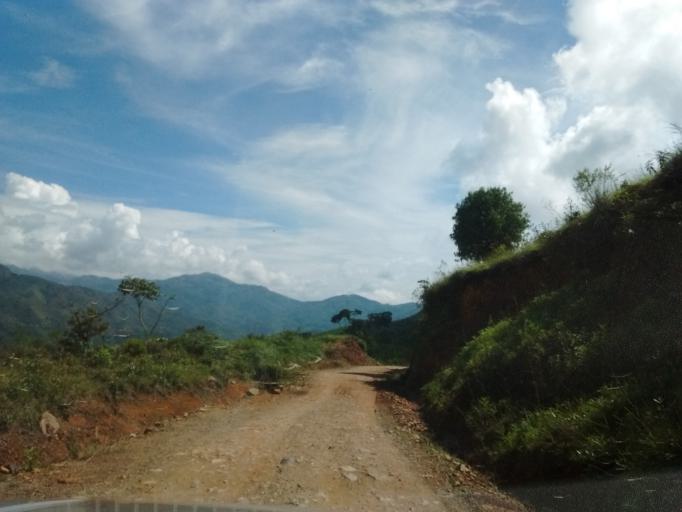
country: CO
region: Cauca
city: Morales
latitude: 2.6878
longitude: -76.7478
